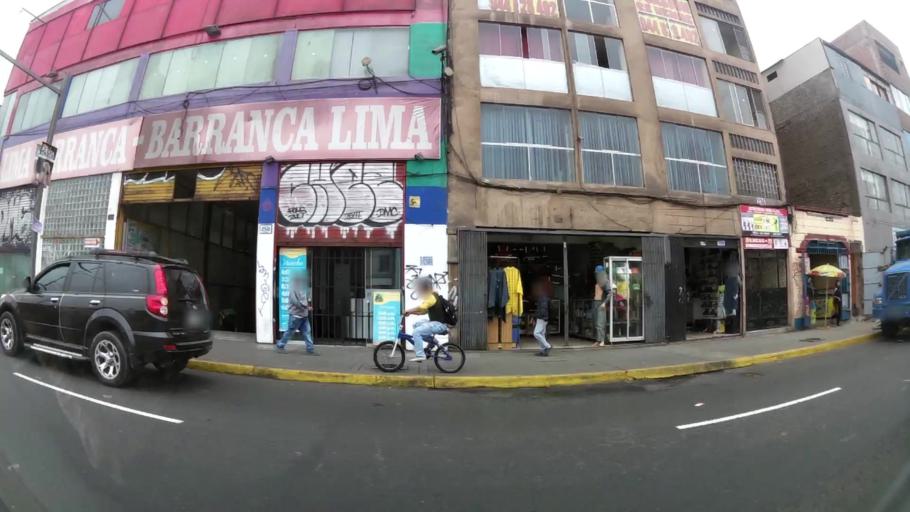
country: PE
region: Lima
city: Lima
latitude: -12.0598
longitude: -77.0324
